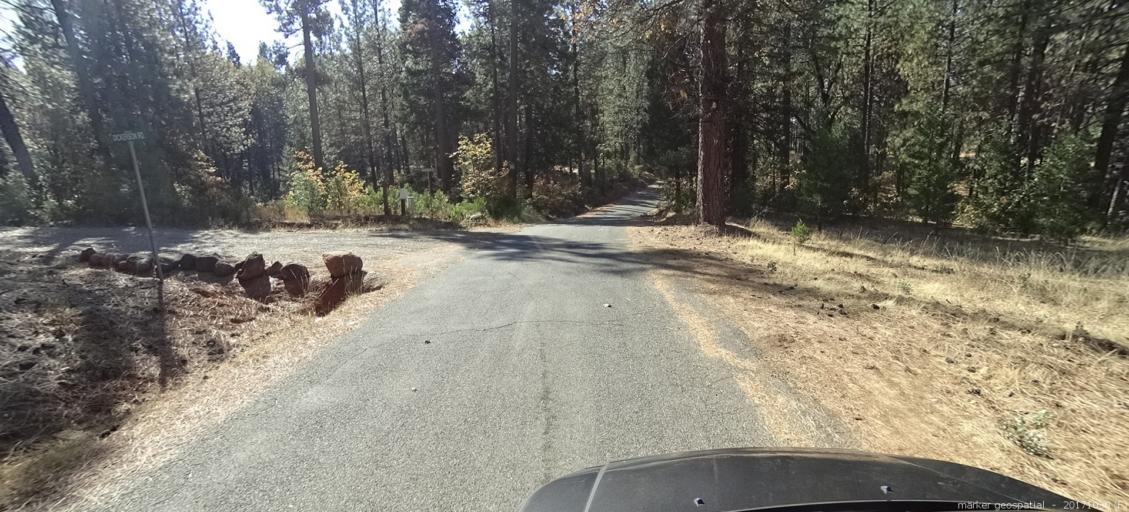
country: US
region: California
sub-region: Shasta County
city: Shingletown
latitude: 40.5955
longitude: -121.8584
